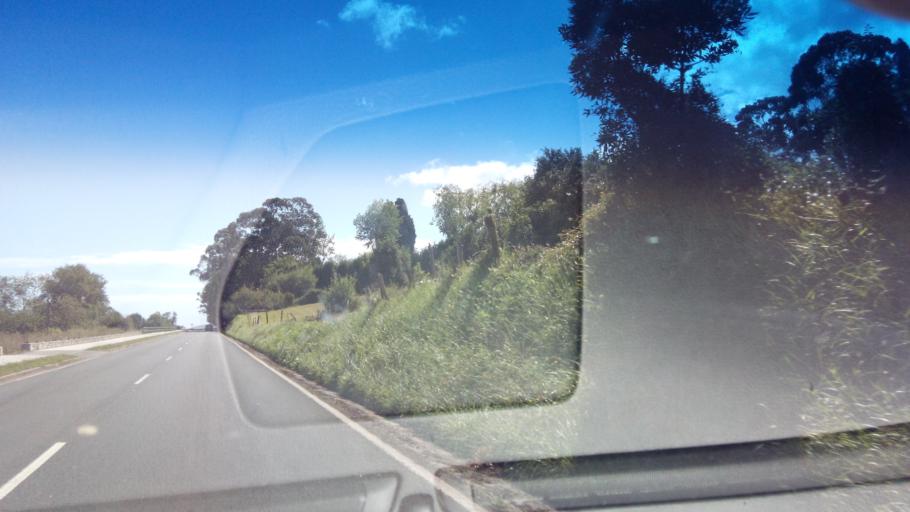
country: ES
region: Asturias
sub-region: Province of Asturias
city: Colunga
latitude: 43.4824
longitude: -5.2432
